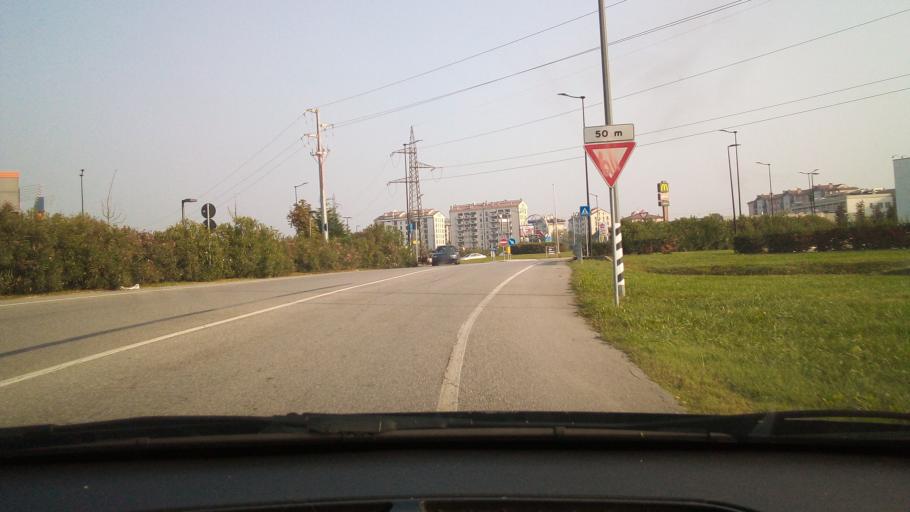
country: IT
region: Lombardy
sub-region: Citta metropolitana di Milano
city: Novegro-Tregarezzo-San Felice
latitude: 45.4851
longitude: 9.2627
